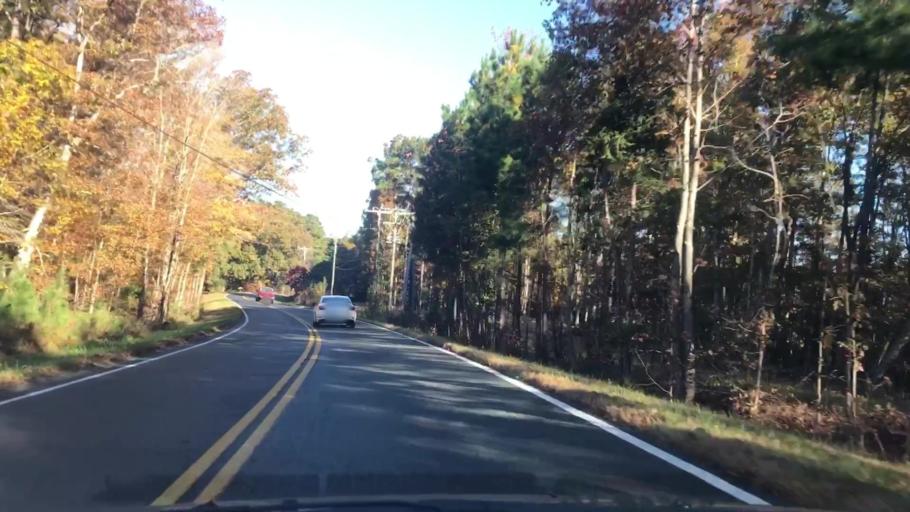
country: US
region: Virginia
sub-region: Henrico County
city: Short Pump
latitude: 37.6412
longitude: -77.6787
